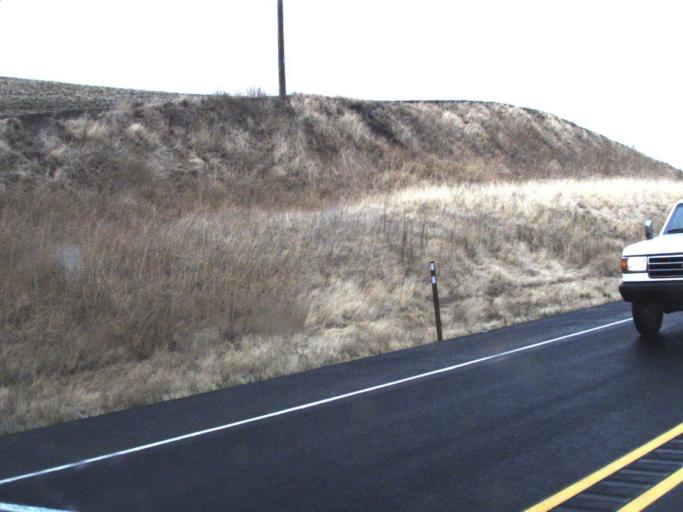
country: US
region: Washington
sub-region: Whitman County
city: Colfax
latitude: 46.9277
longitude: -117.3419
